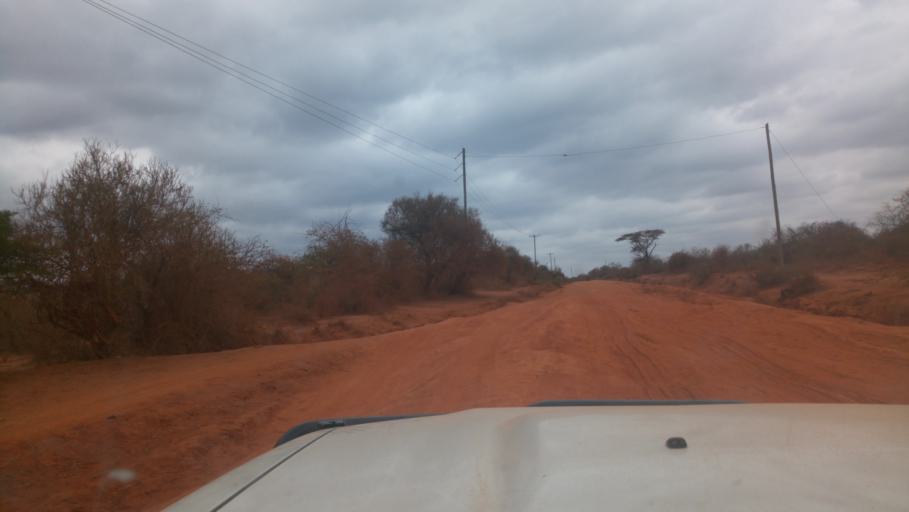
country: KE
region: Makueni
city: Wote
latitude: -1.9091
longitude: 38.0206
